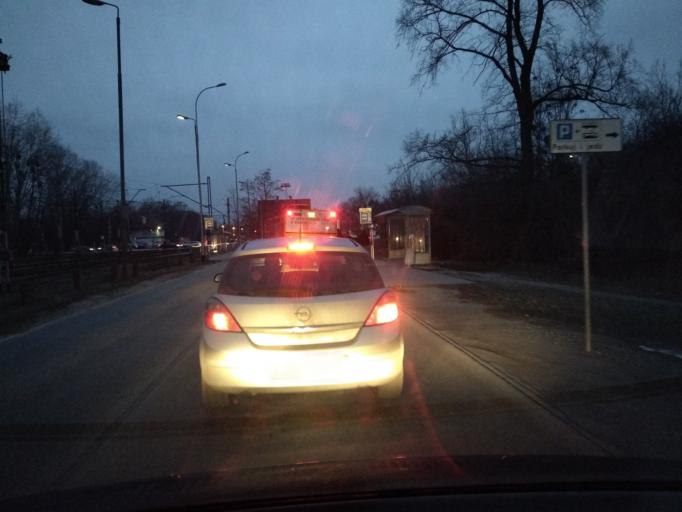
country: PL
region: Lower Silesian Voivodeship
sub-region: Powiat wroclawski
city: Wroclaw
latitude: 51.1260
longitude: 16.9553
